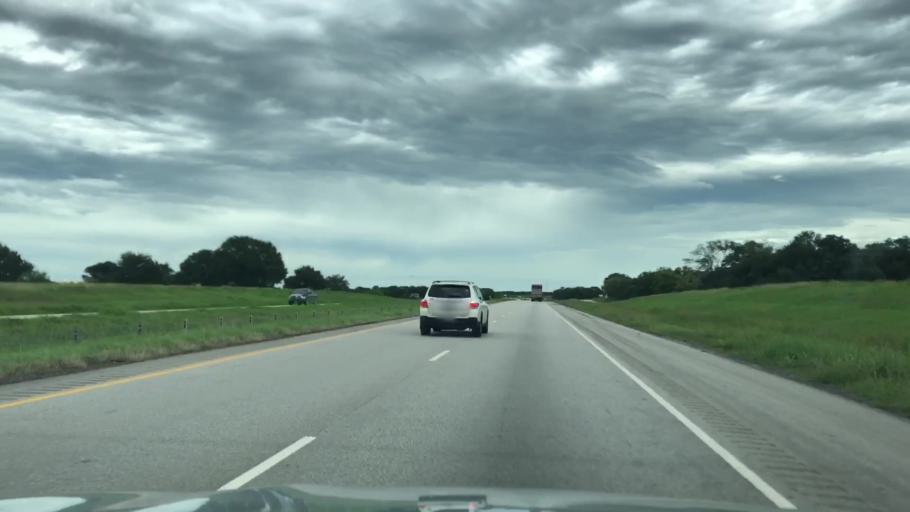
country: US
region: Texas
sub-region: Colorado County
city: Weimar
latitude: 29.6901
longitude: -96.7157
